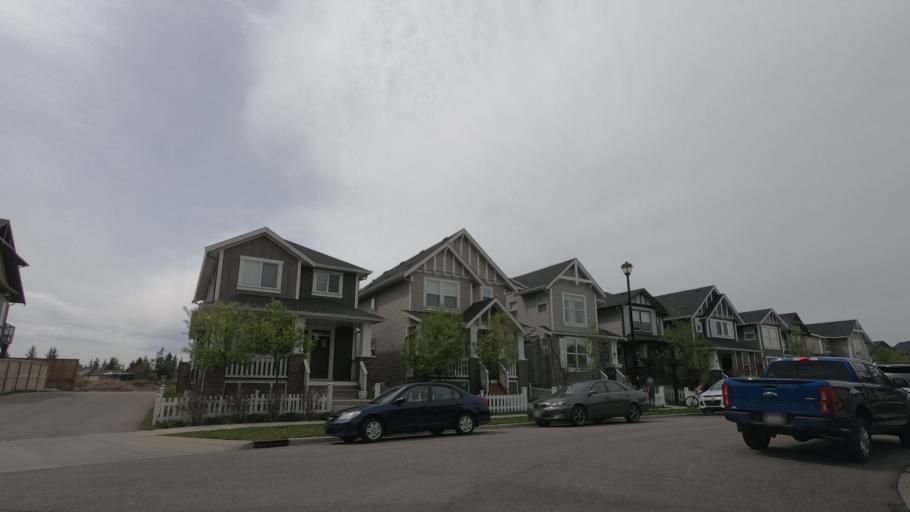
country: CA
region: Alberta
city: Airdrie
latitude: 51.3013
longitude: -114.0360
